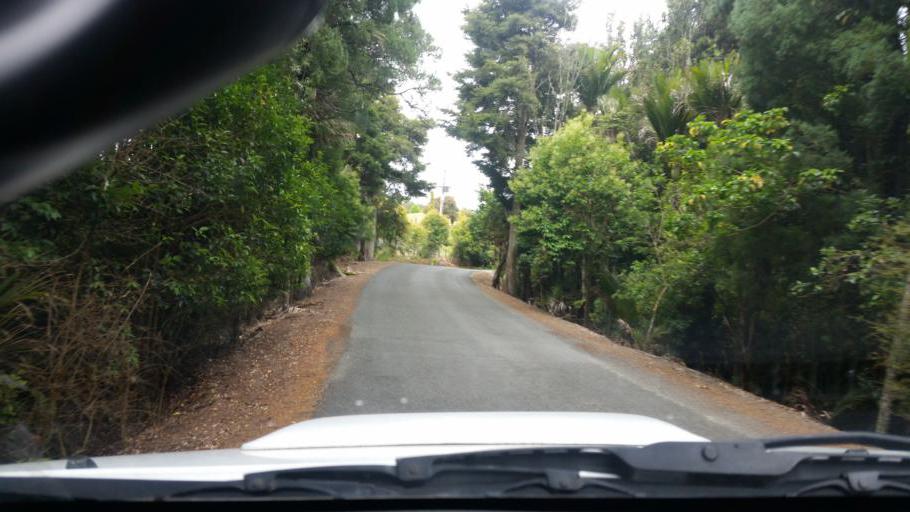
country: NZ
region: Northland
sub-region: Whangarei
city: Ruakaka
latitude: -36.0963
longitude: 174.3527
